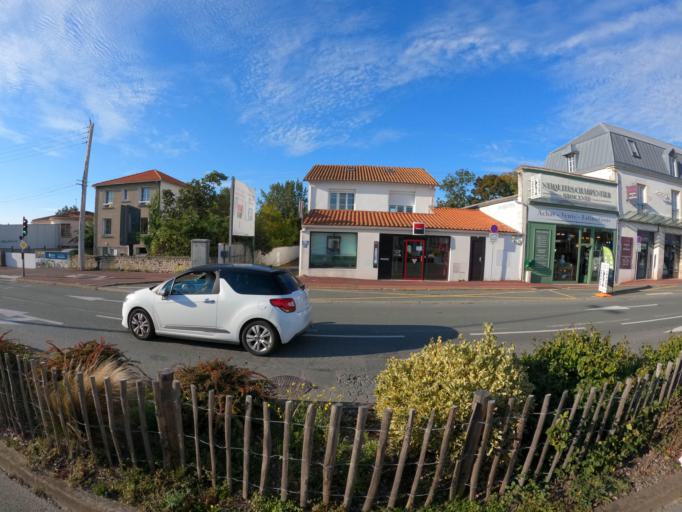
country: FR
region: Poitou-Charentes
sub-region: Departement de la Charente-Maritime
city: Puilboreau
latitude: 46.1695
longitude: -1.1290
